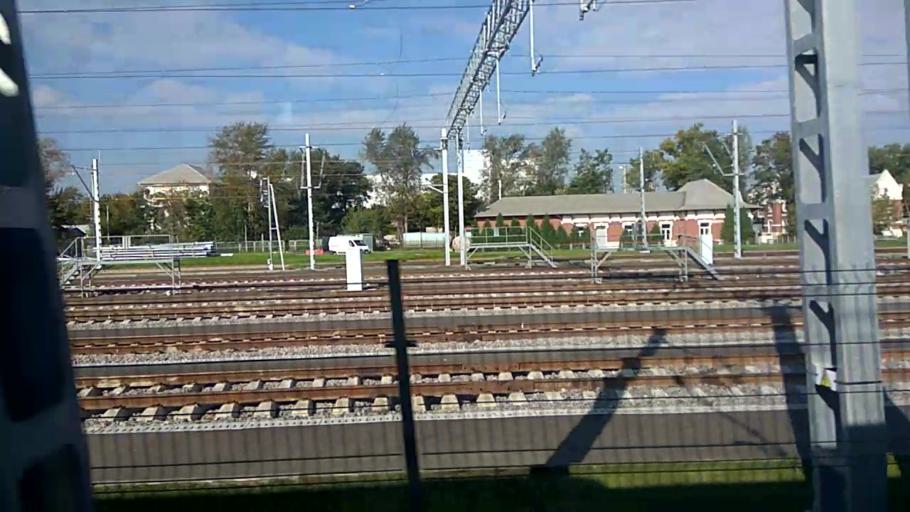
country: RU
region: Moscow
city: Ryazanskiy
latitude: 55.7405
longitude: 37.7340
